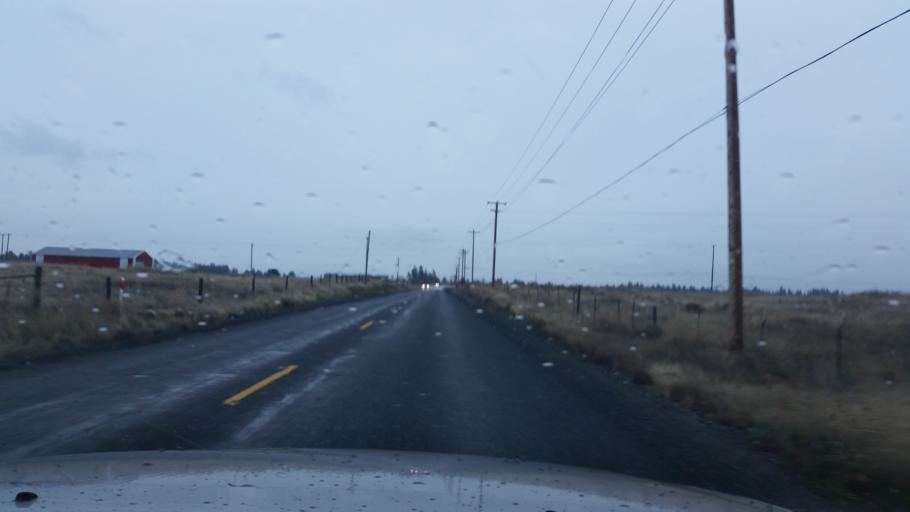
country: US
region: Washington
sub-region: Spokane County
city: Airway Heights
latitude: 47.6719
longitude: -117.5641
